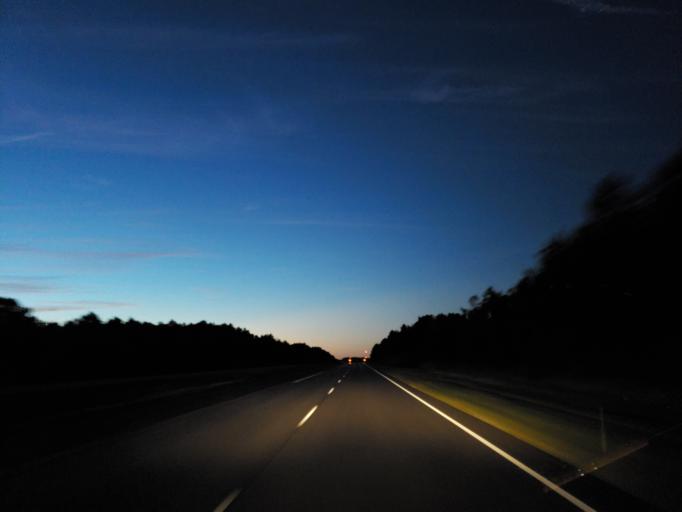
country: US
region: Mississippi
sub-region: Clarke County
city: Quitman
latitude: 32.0850
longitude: -88.6950
